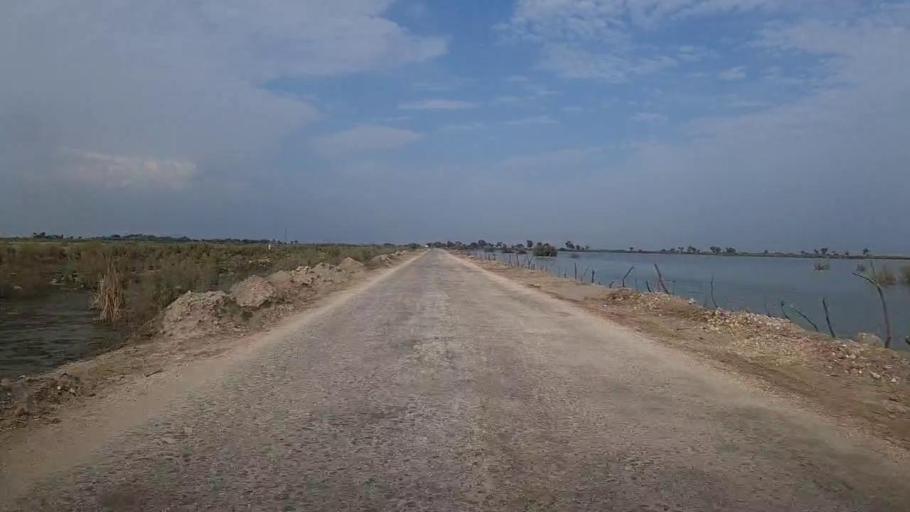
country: PK
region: Sindh
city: Thul
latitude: 28.2764
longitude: 68.8457
